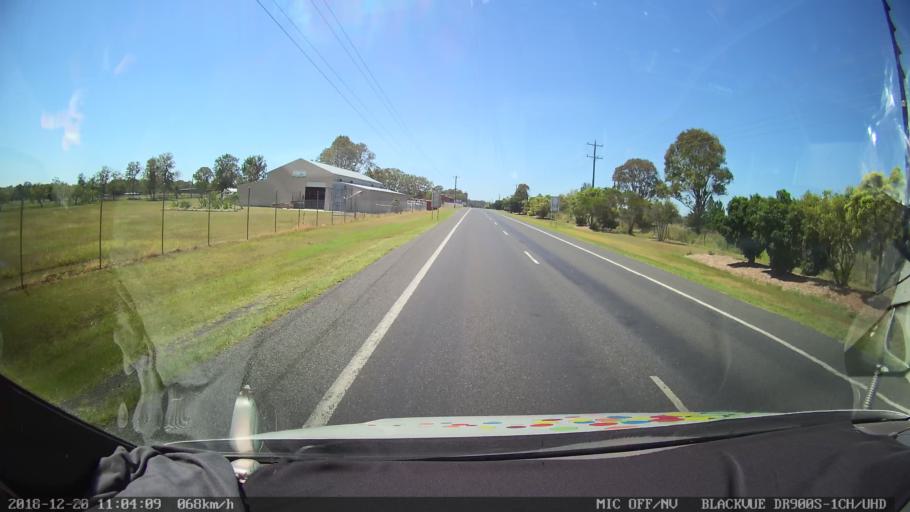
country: AU
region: New South Wales
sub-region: Richmond Valley
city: Casino
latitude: -28.8825
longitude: 153.0440
